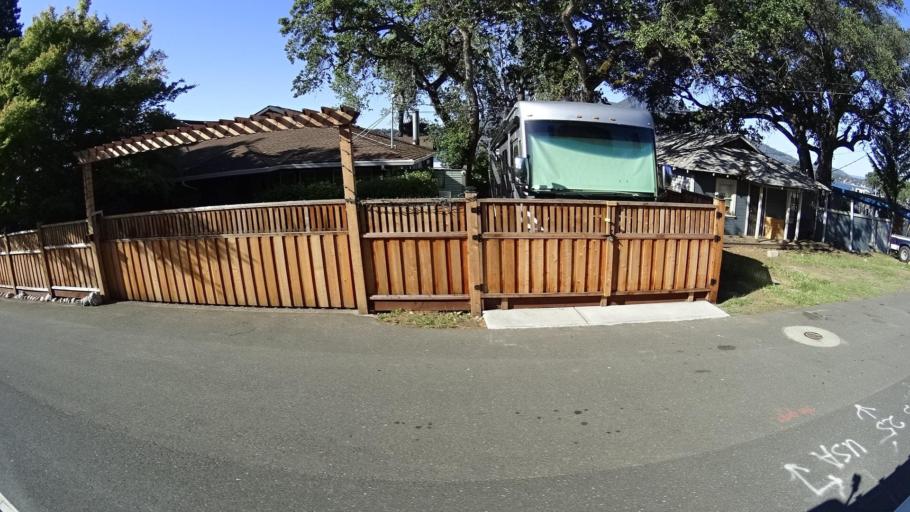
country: US
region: California
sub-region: Lake County
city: Clearlake Oaks
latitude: 39.0236
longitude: -122.7199
